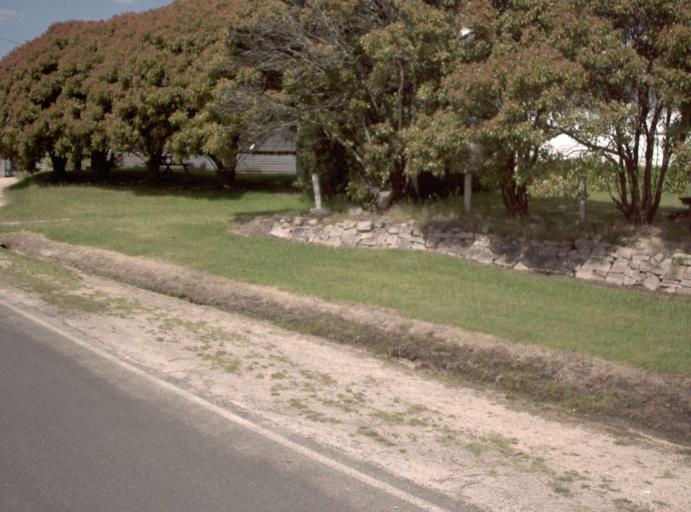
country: AU
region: New South Wales
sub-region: Bega Valley
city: Eden
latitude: -37.4754
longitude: 149.5911
